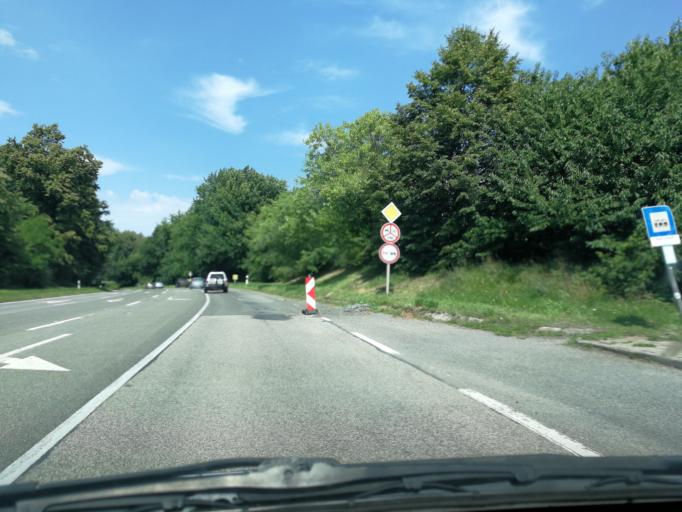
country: HU
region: Baranya
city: Mecseknadasd
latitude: 46.1952
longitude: 18.4538
